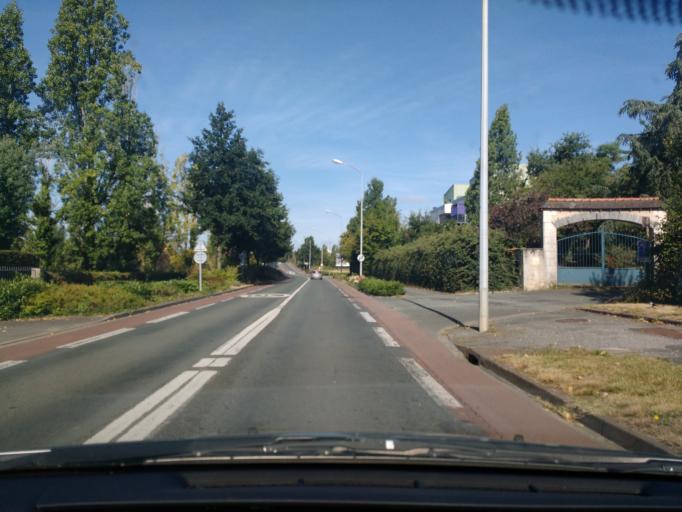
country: FR
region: Pays de la Loire
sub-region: Departement de Maine-et-Loire
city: Angers
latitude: 47.4691
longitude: -0.5086
